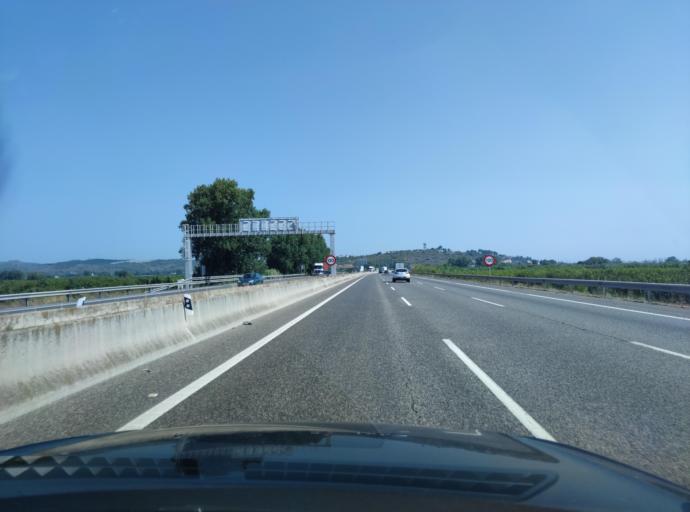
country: ES
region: Valencia
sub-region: Provincia de Valencia
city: Beneixida
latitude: 39.0726
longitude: -0.5418
